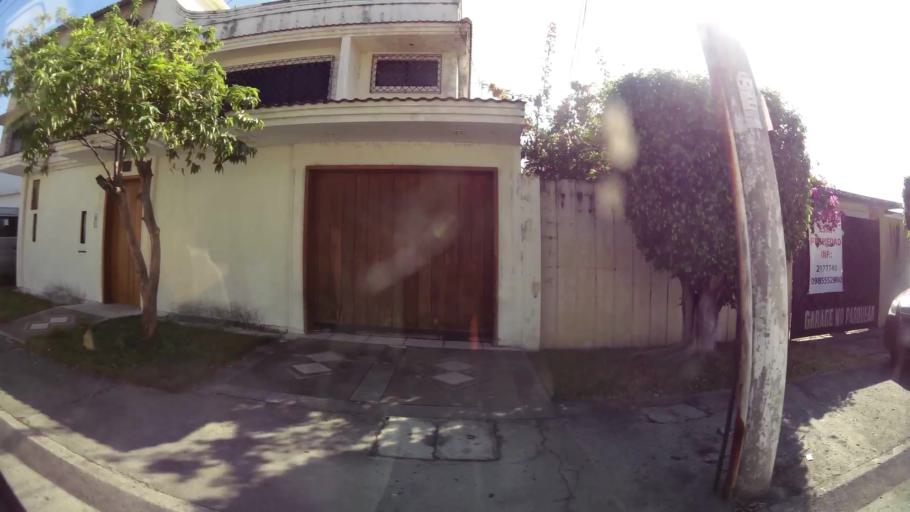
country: EC
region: Guayas
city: Guayaquil
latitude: -2.1689
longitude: -79.9031
